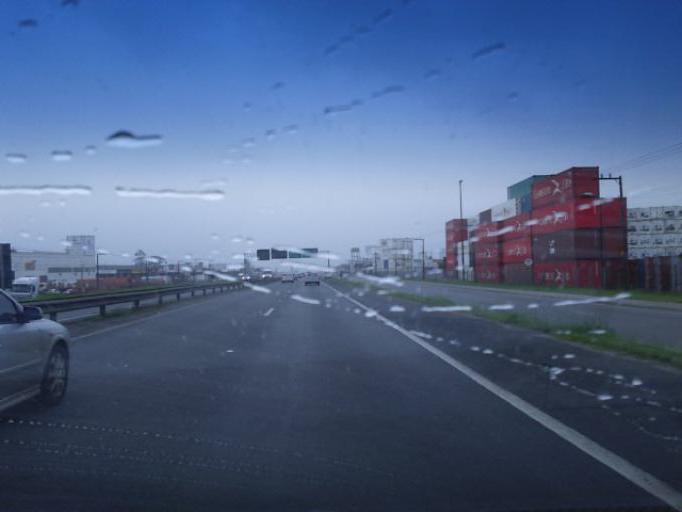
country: BR
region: Santa Catarina
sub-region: Itajai
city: Itajai
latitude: -26.8801
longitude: -48.7254
